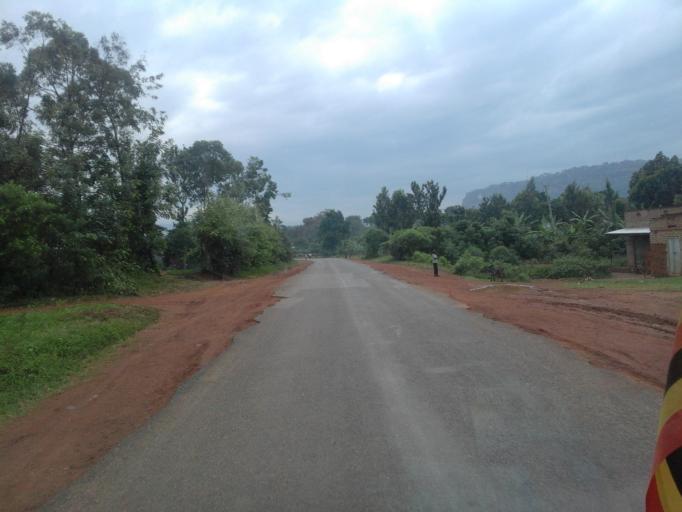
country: UG
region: Eastern Region
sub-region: Sironko District
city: Sironko
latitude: 1.2071
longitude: 34.2097
